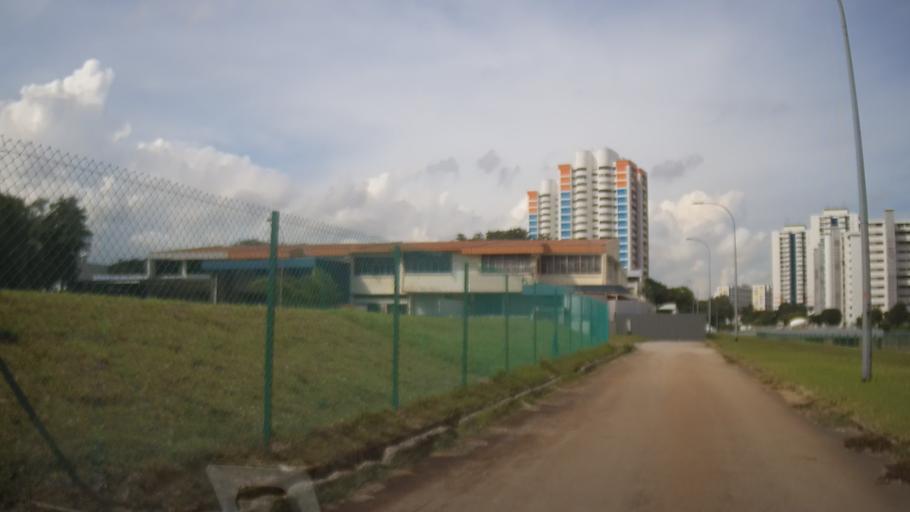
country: SG
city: Singapore
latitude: 1.3221
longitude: 103.8794
